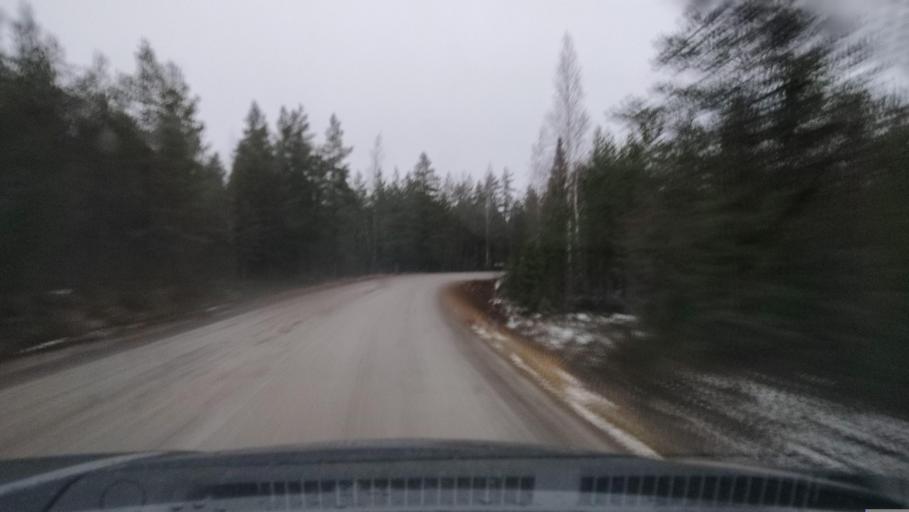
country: FI
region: Southern Ostrobothnia
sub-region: Suupohja
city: Karijoki
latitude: 62.1312
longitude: 21.6198
